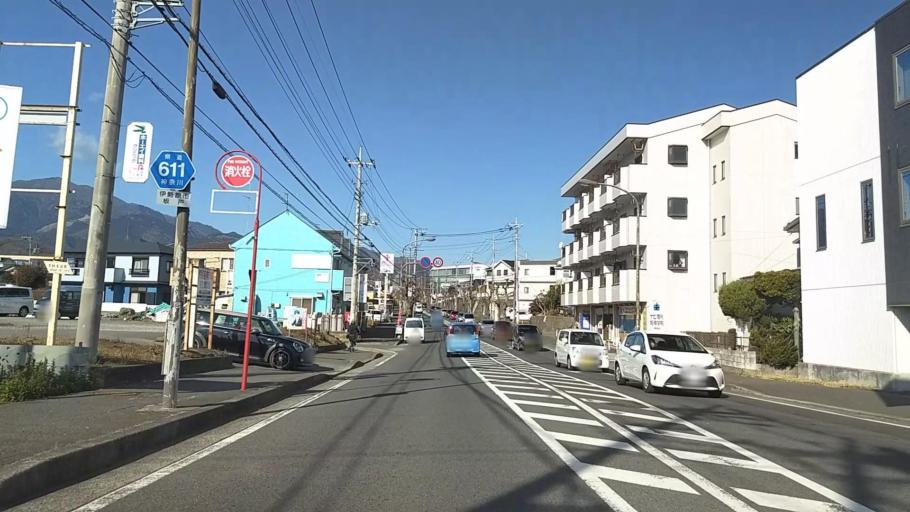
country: JP
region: Kanagawa
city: Isehara
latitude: 35.3993
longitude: 139.2986
